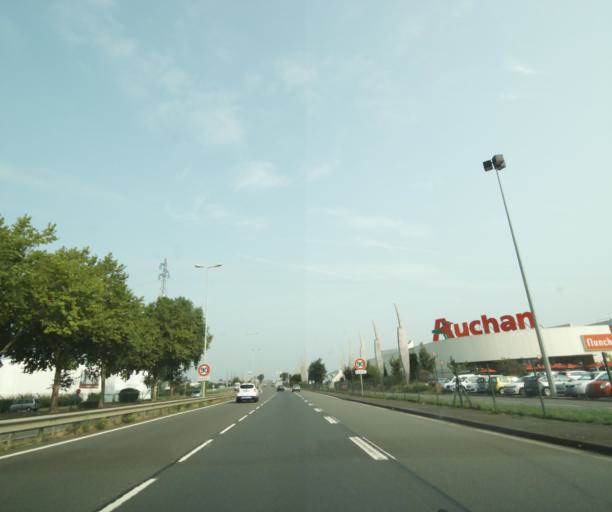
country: FR
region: Pays de la Loire
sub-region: Departement de la Sarthe
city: La Chapelle-Saint-Aubin
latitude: 48.0413
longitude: 0.1742
